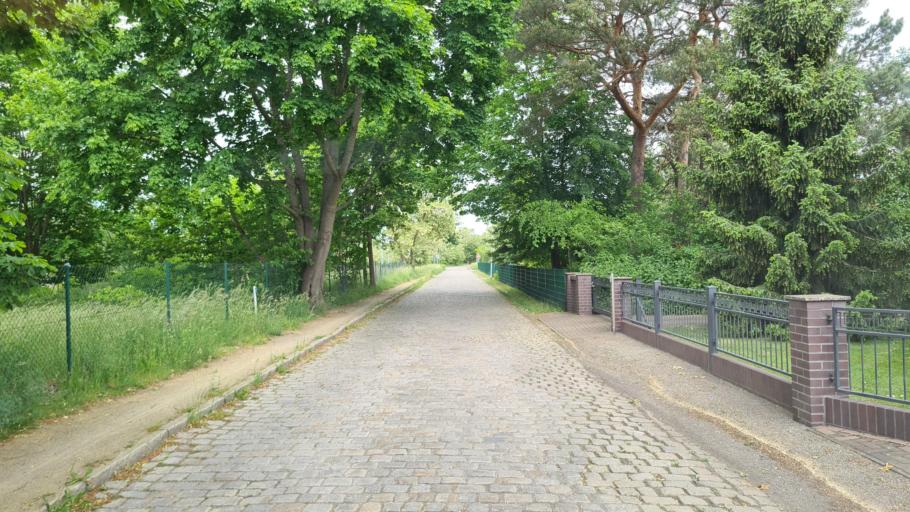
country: DE
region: Brandenburg
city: Grossraschen
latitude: 51.5882
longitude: 14.0163
